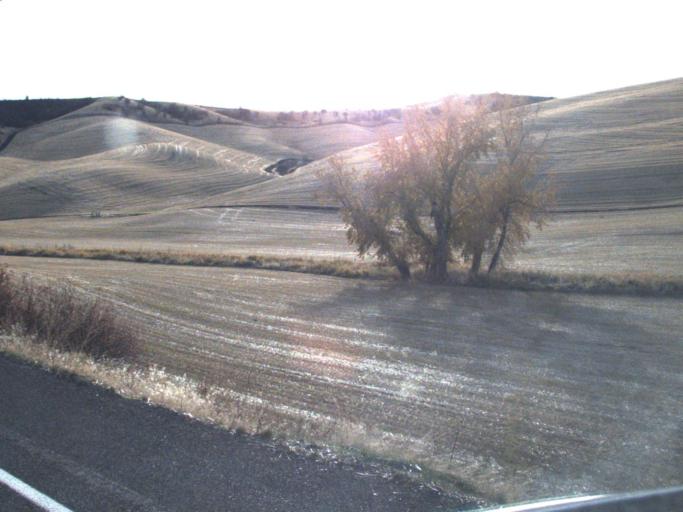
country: US
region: Washington
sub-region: Columbia County
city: Dayton
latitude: 46.3389
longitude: -117.9794
